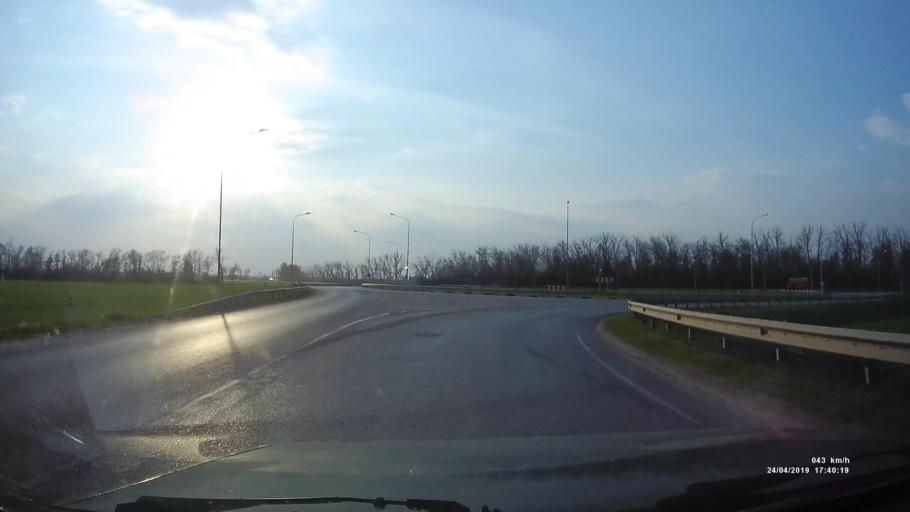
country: RU
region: Rostov
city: Tselina
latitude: 46.5322
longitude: 40.9894
